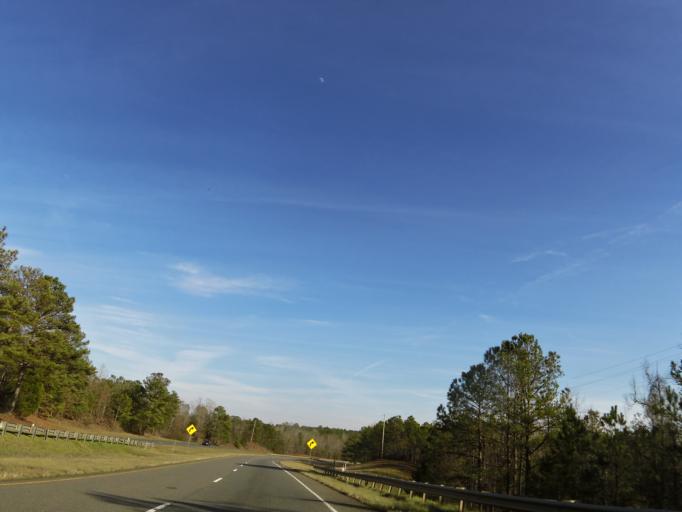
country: US
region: Georgia
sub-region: Stewart County
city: Richland
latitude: 32.1516
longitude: -84.6931
